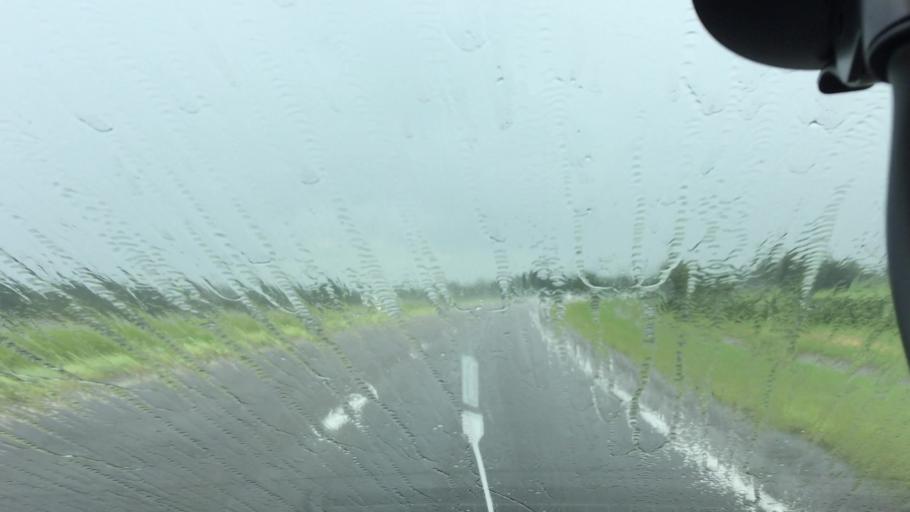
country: US
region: Alabama
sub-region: Montgomery County
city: Pike Road
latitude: 32.2290
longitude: -86.1199
